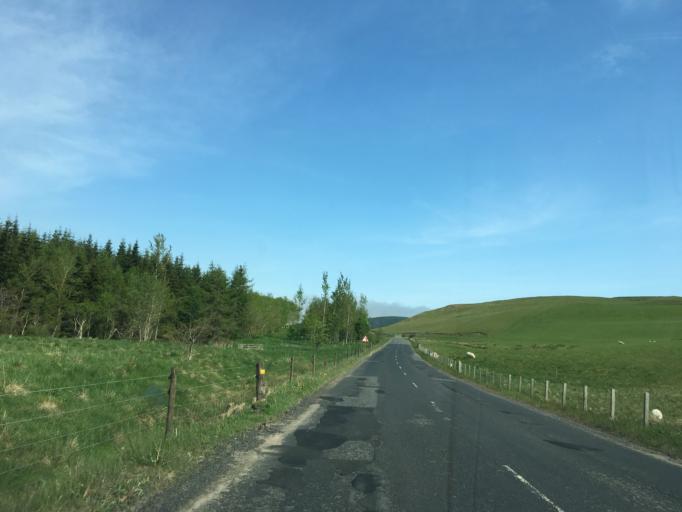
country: GB
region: Scotland
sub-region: South Lanarkshire
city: Biggar
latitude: 55.6430
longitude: -3.4271
